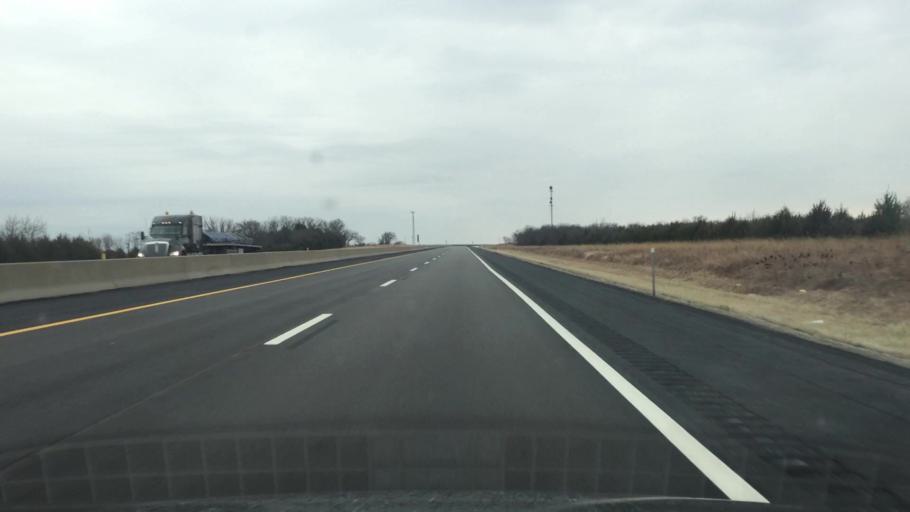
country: US
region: Kansas
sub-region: Shawnee County
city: Auburn
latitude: 38.8479
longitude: -95.8644
